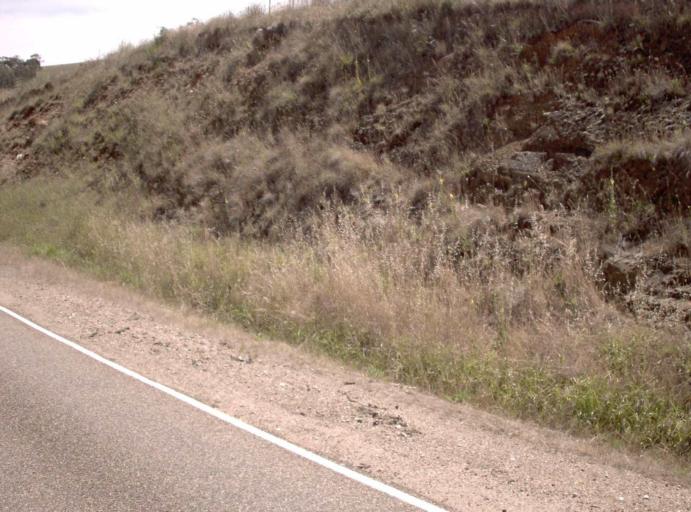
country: AU
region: Victoria
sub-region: Alpine
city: Mount Beauty
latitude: -37.0678
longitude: 147.6031
